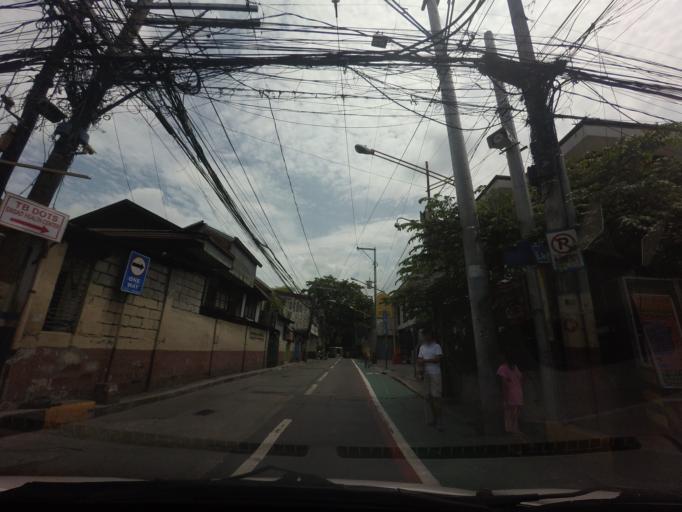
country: PH
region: Calabarzon
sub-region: Province of Rizal
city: Pateros
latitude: 14.5655
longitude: 121.0802
